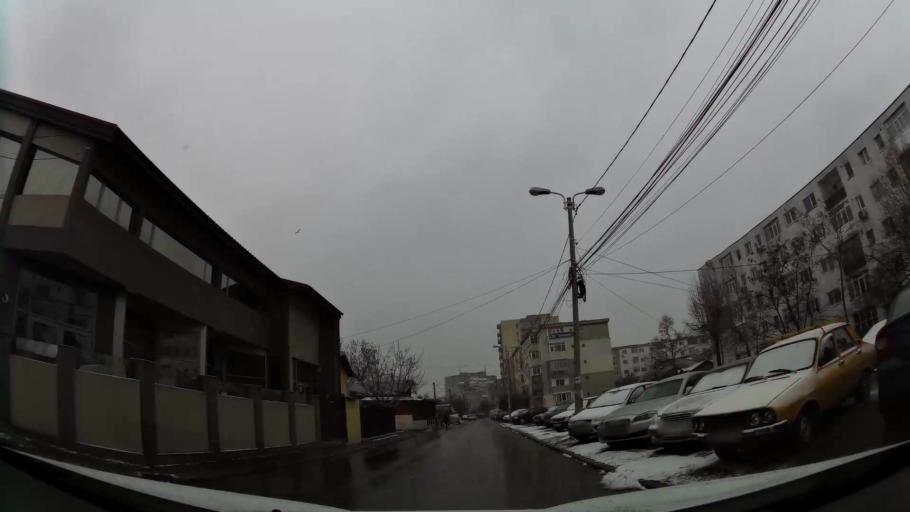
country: RO
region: Prahova
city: Ploiesti
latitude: 44.9472
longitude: 25.9984
